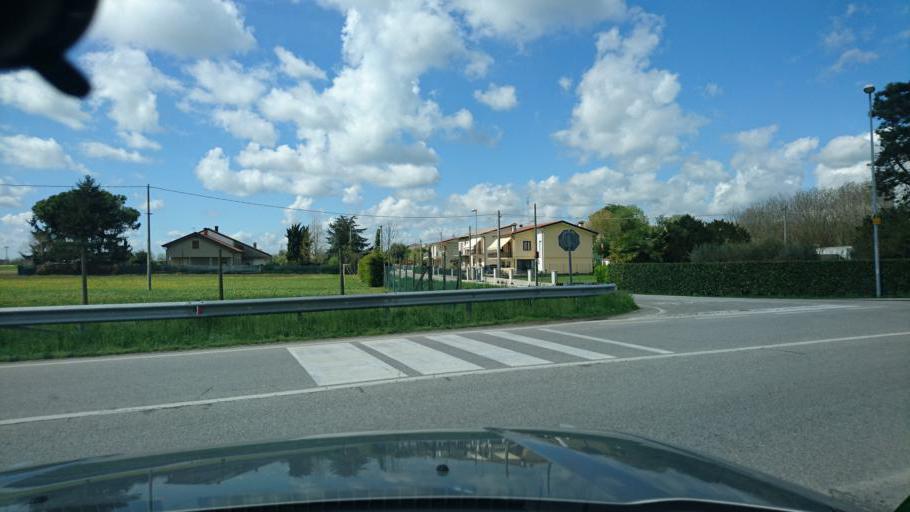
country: IT
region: Veneto
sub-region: Provincia di Padova
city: Tremignon
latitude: 45.5238
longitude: 11.7987
